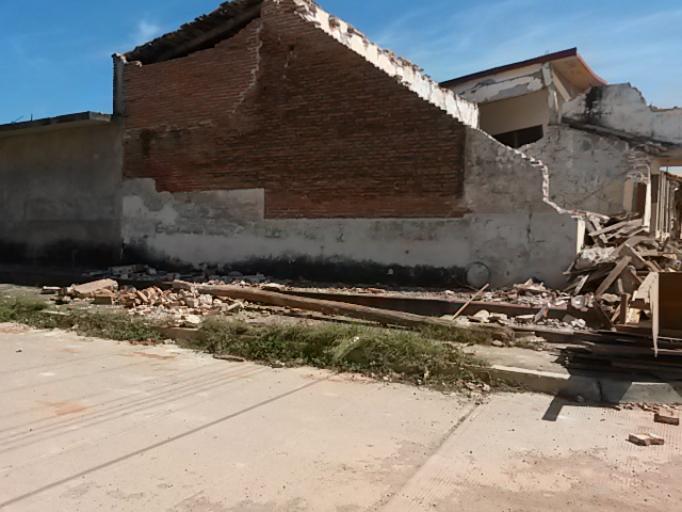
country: MX
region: Oaxaca
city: Asuncion Ixtaltepec
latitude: 16.5054
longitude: -95.0572
